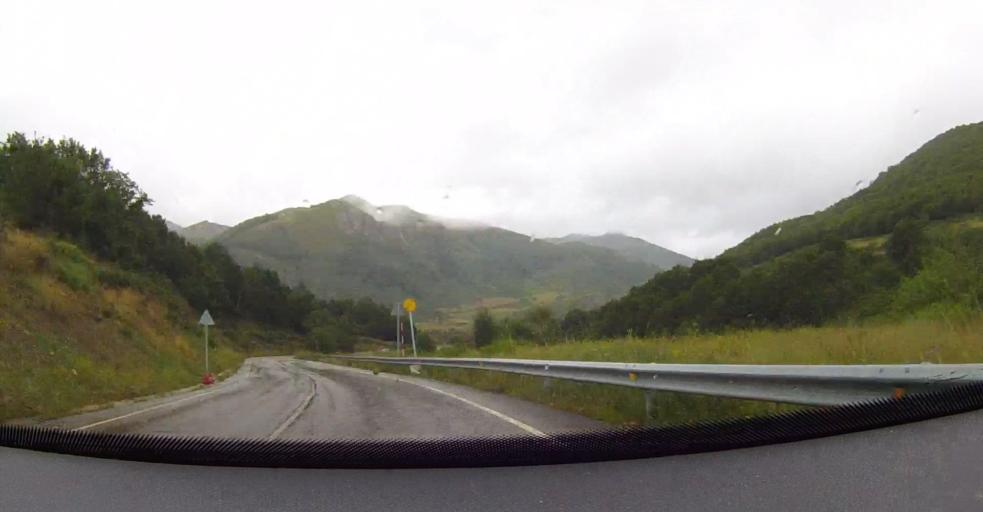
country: ES
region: Castille and Leon
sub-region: Provincia de Leon
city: Marana
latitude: 43.0713
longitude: -5.1619
